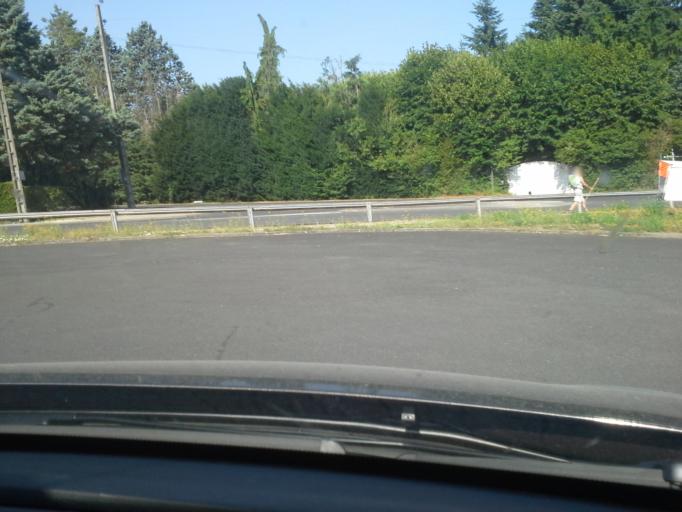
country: FR
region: Centre
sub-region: Departement du Loir-et-Cher
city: Chailles
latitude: 47.5244
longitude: 1.3029
